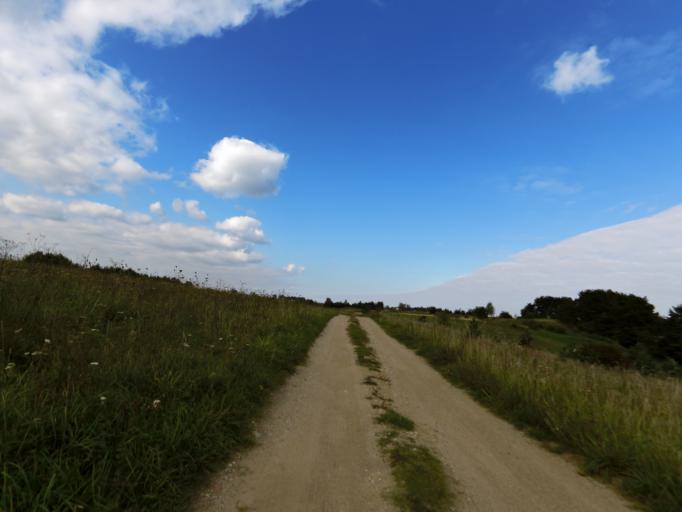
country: LT
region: Vilnius County
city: Pilaite
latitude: 54.7070
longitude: 25.1514
